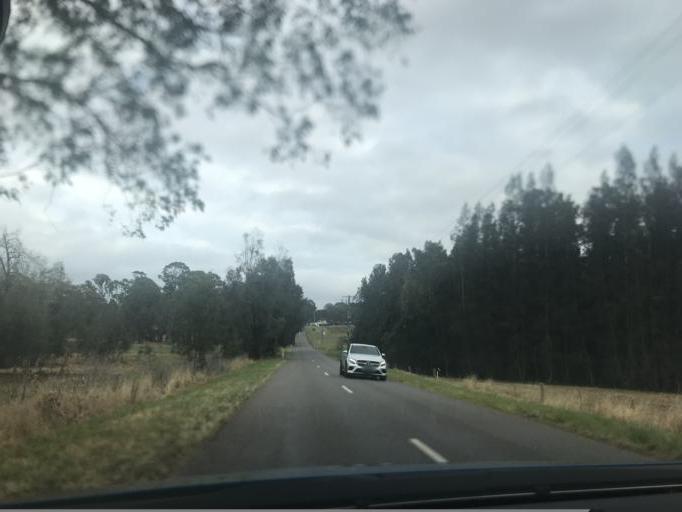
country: AU
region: New South Wales
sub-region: Cessnock
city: Cessnock
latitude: -32.8124
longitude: 151.3154
